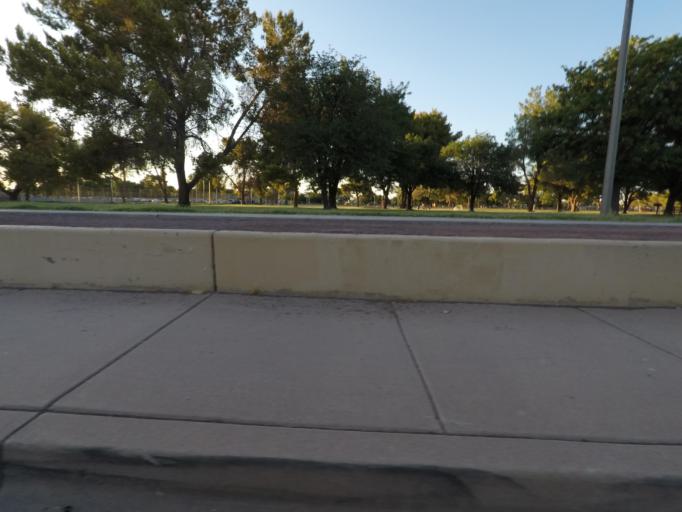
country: US
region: Arizona
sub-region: Maricopa County
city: Glendale
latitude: 33.5022
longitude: -112.1319
